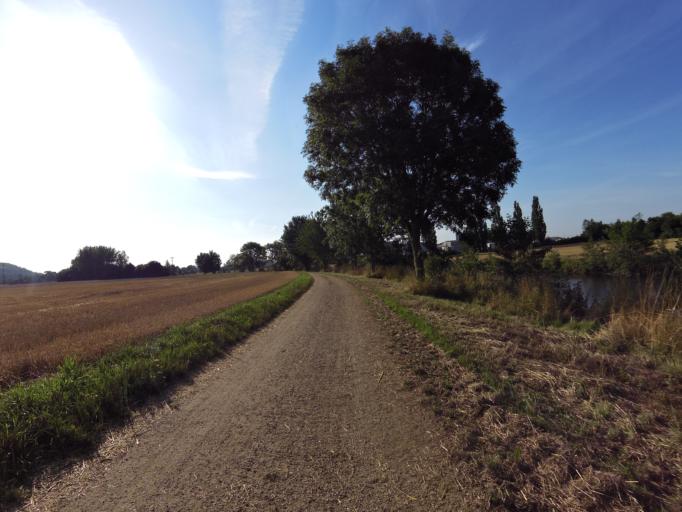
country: DE
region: North Rhine-Westphalia
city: Huckelhoven
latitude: 51.0545
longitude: 6.1840
